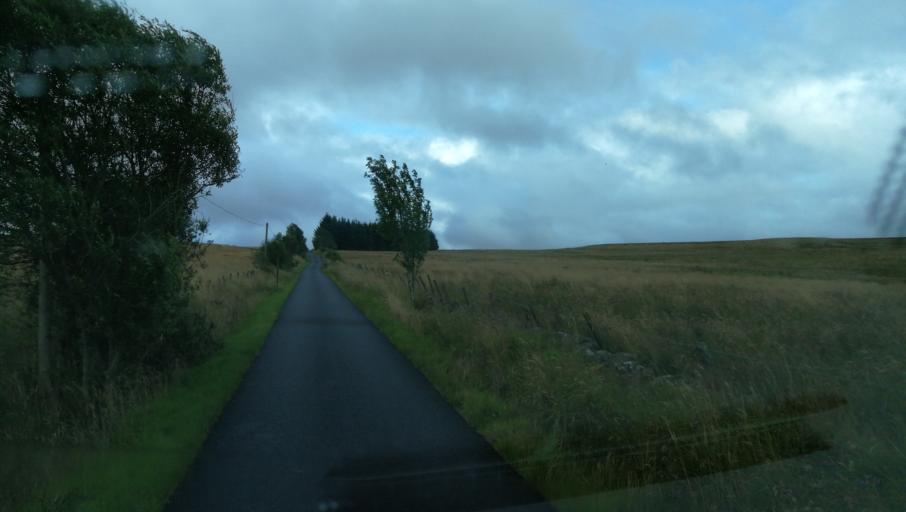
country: GB
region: Scotland
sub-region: Perth and Kinross
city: Blairgowrie
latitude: 56.6873
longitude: -3.3855
